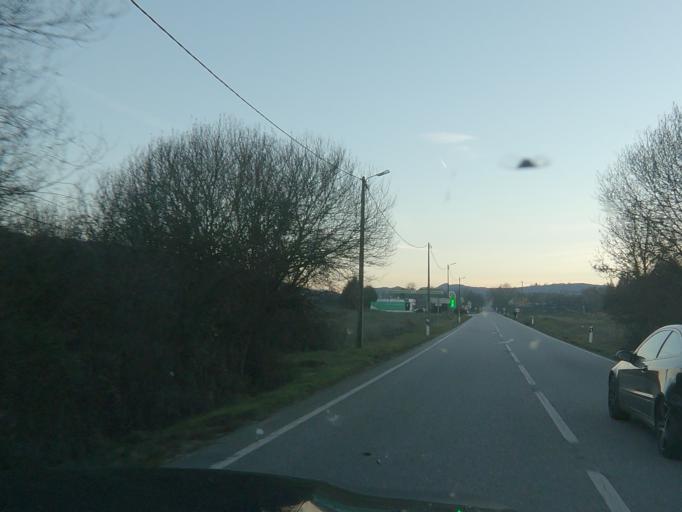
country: PT
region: Vila Real
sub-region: Vila Pouca de Aguiar
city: Vila Pouca de Aguiar
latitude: 41.4367
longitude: -7.6772
